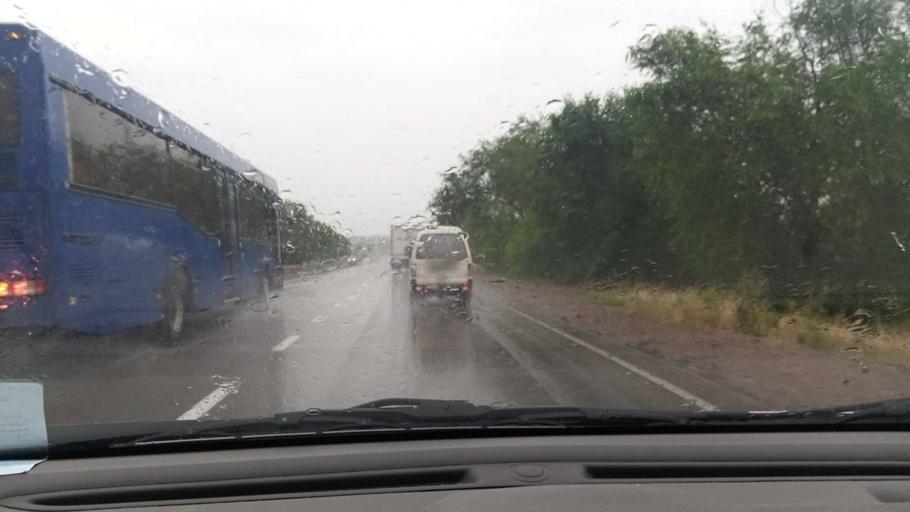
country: UZ
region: Toshkent
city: Angren
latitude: 40.9579
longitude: 69.9365
